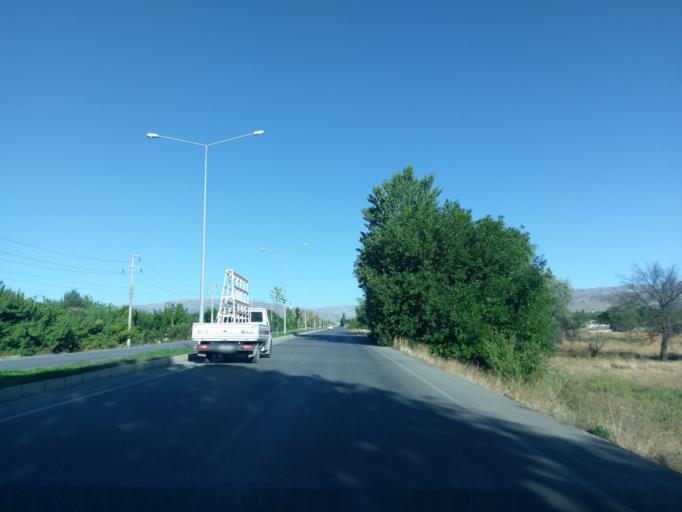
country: TR
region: Erzincan
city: Erzincan
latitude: 39.7706
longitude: 39.4258
